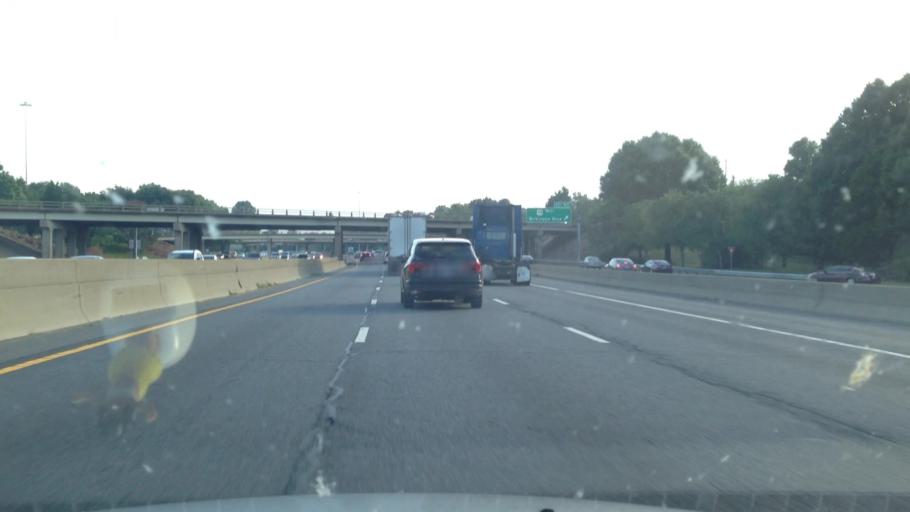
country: US
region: North Carolina
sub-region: Mecklenburg County
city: Charlotte
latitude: 35.2261
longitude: -80.8637
